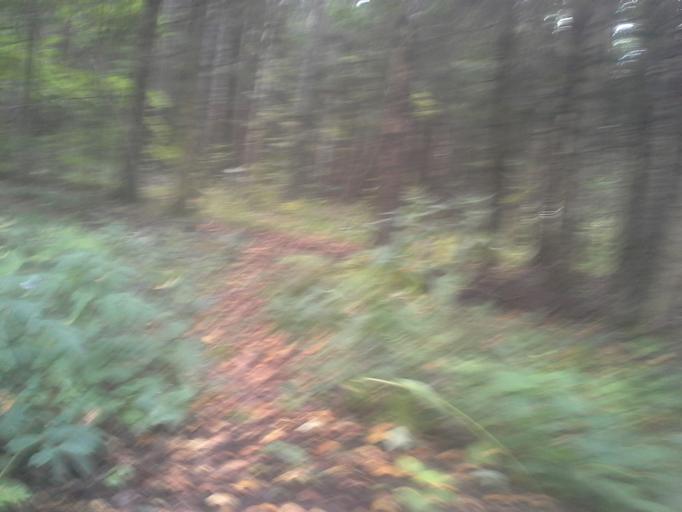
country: RU
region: Moskovskaya
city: Kievskij
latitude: 55.3490
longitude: 36.9600
